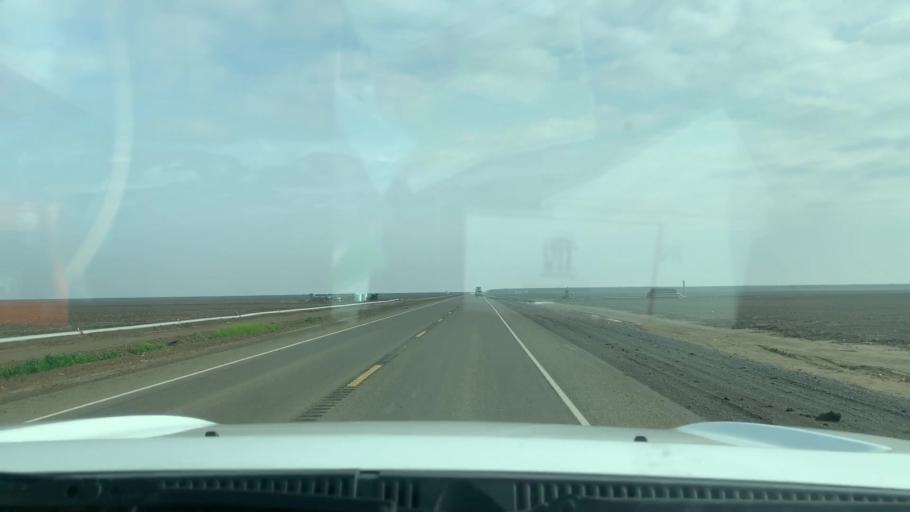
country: US
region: California
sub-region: Fresno County
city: Huron
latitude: 36.2553
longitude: -120.0234
